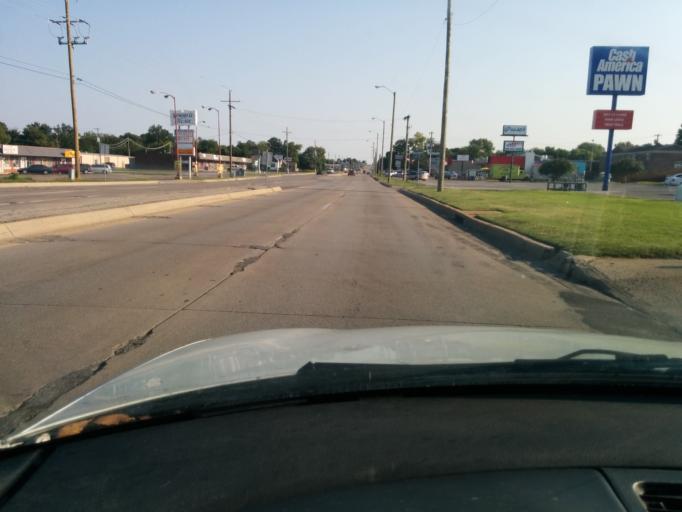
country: US
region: Oklahoma
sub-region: Tulsa County
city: Tulsa
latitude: 36.1475
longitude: -95.8868
